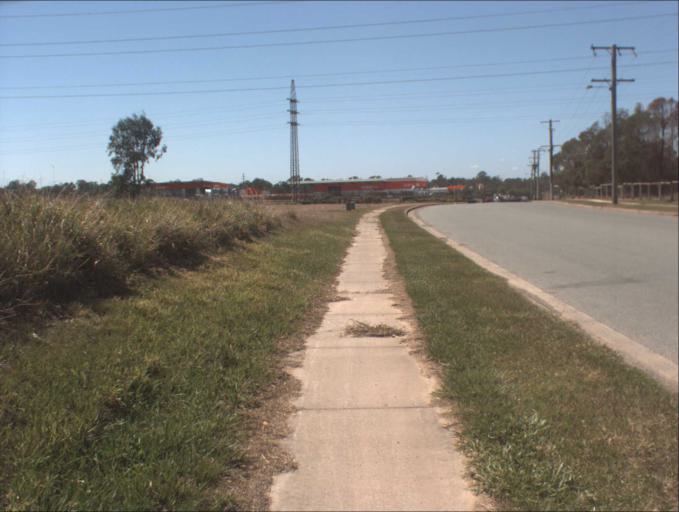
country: AU
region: Queensland
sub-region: Logan
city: Waterford West
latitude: -27.6687
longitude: 153.1144
